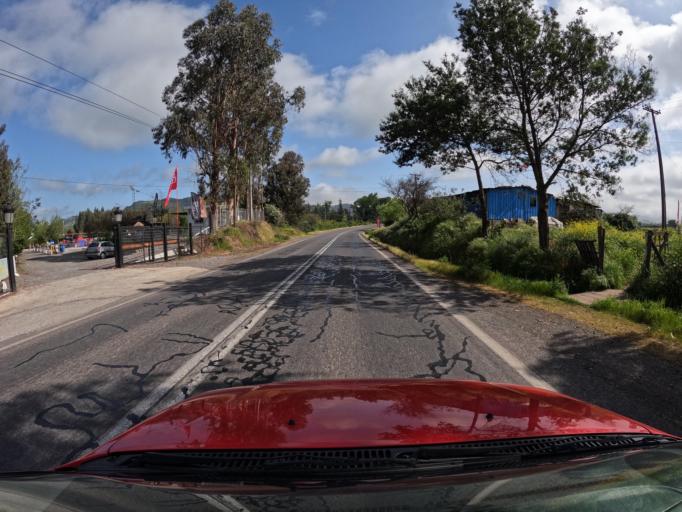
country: CL
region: Maule
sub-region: Provincia de Curico
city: Teno
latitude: -34.8550
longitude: -71.1919
